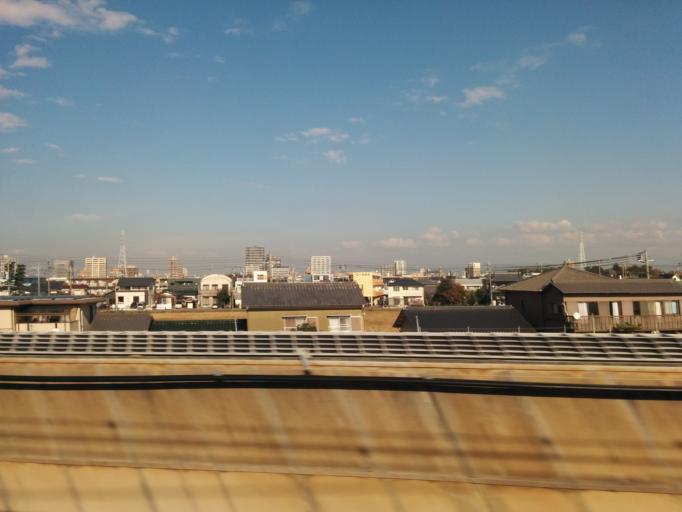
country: JP
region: Aichi
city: Anjo
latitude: 34.9468
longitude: 137.0810
